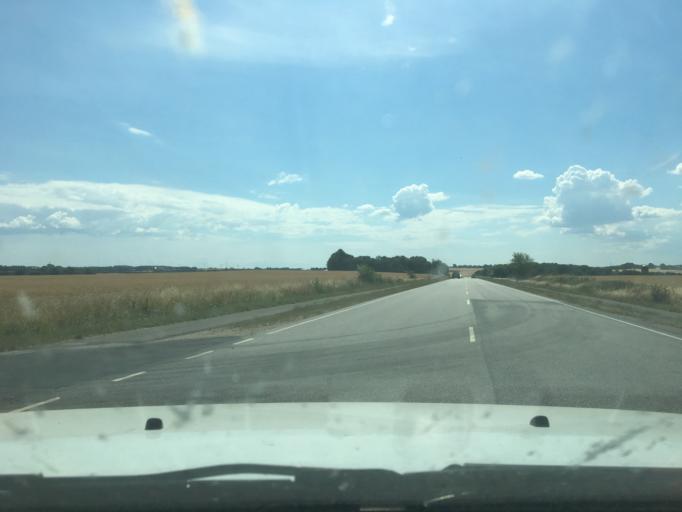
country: DK
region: Central Jutland
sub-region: Favrskov Kommune
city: Hadsten
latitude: 56.3587
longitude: 10.0975
